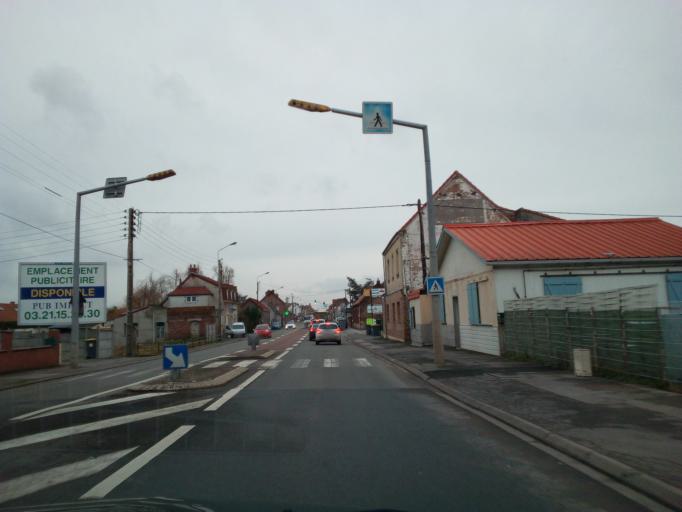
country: FR
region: Nord-Pas-de-Calais
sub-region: Departement du Pas-de-Calais
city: Annequin
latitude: 50.5101
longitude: 2.7308
